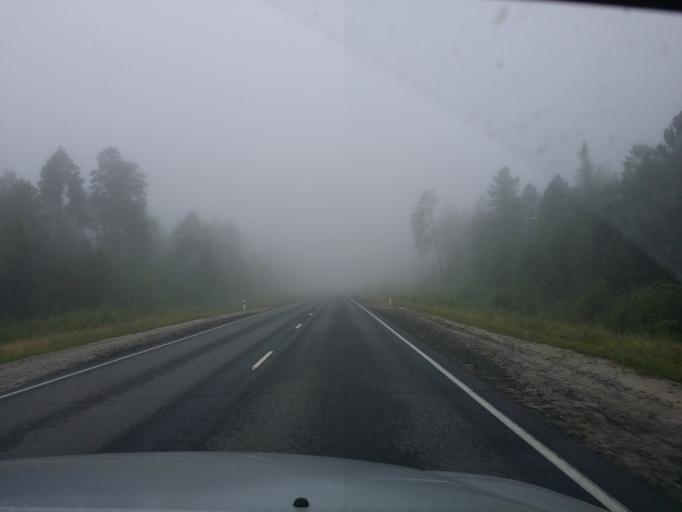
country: RU
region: Khanty-Mansiyskiy Avtonomnyy Okrug
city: Gornopravdinsk
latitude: 59.6603
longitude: 69.9610
